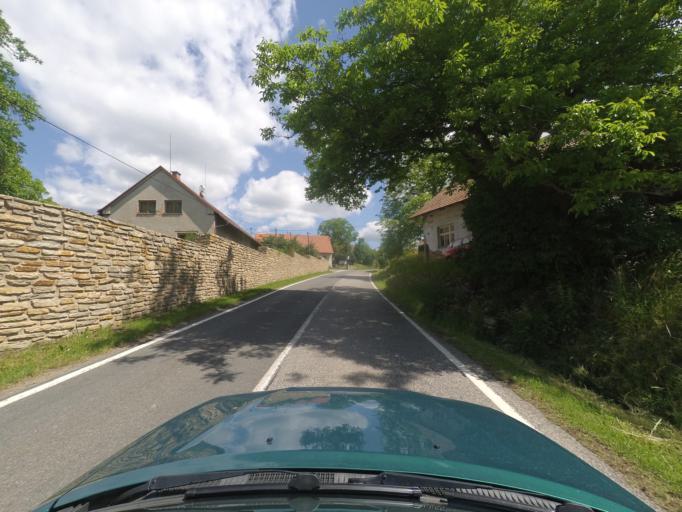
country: CZ
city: Dobruska
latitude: 50.3081
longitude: 16.1847
